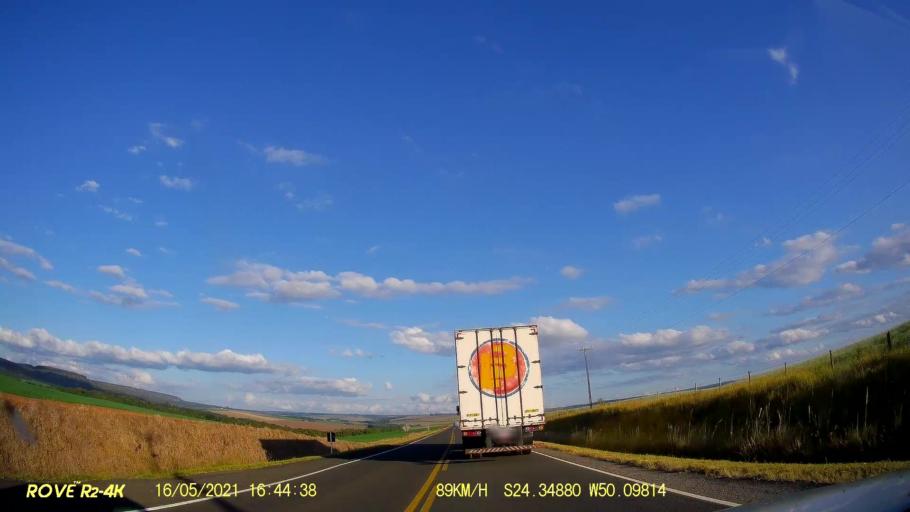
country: BR
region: Parana
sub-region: Pirai Do Sul
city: Pirai do Sul
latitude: -24.3489
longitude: -50.0981
